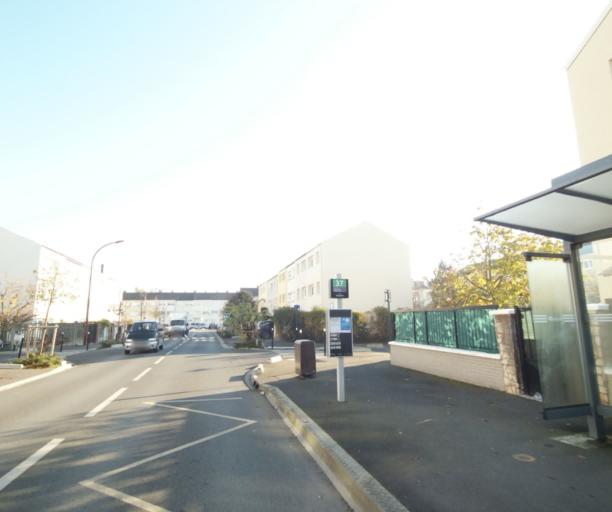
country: FR
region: Ile-de-France
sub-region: Departement du Val-d'Oise
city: Arnouville
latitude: 48.9960
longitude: 2.4269
